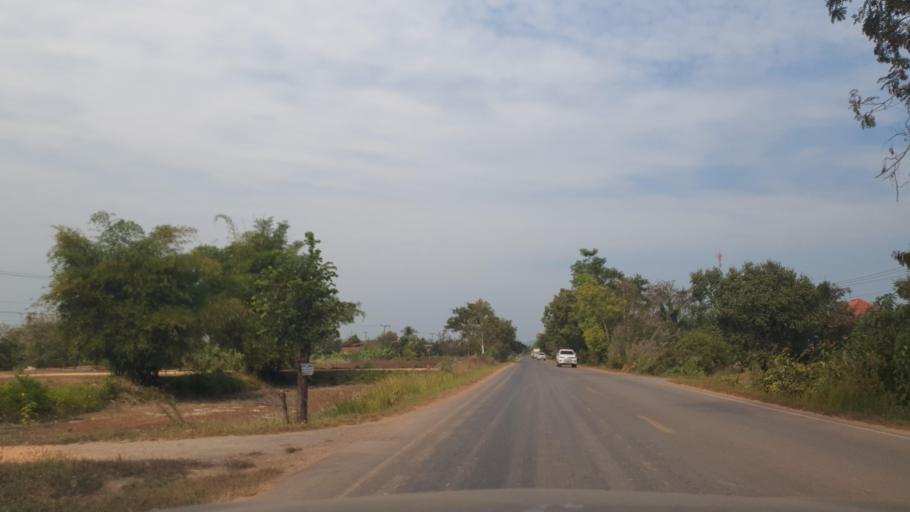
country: TH
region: Changwat Bueng Kan
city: Bung Khla
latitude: 18.1940
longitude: 104.0539
